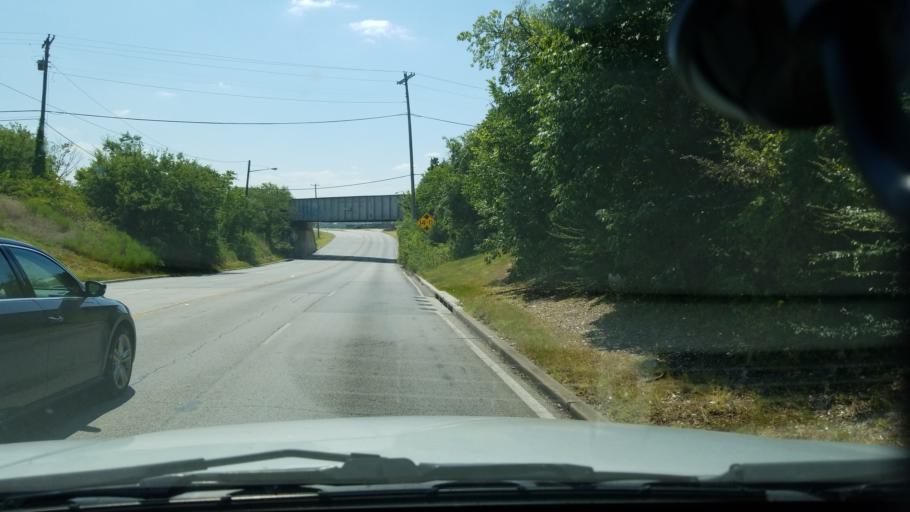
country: US
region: Texas
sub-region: Dallas County
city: Grand Prairie
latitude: 32.7486
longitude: -96.9539
